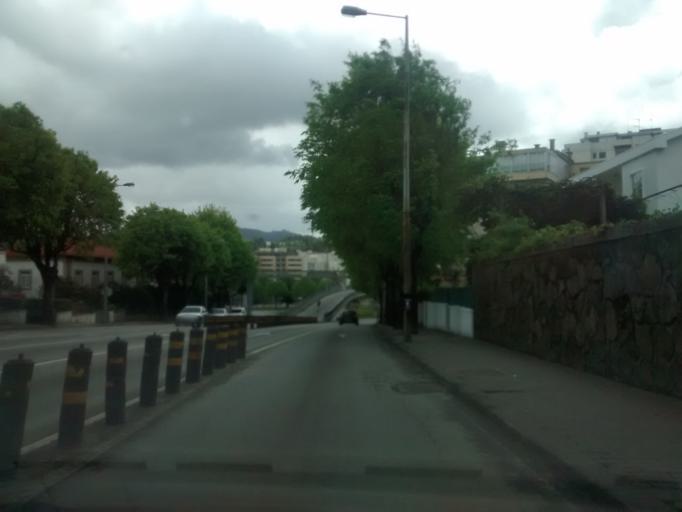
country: PT
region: Braga
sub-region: Braga
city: Braga
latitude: 41.5437
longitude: -8.4327
